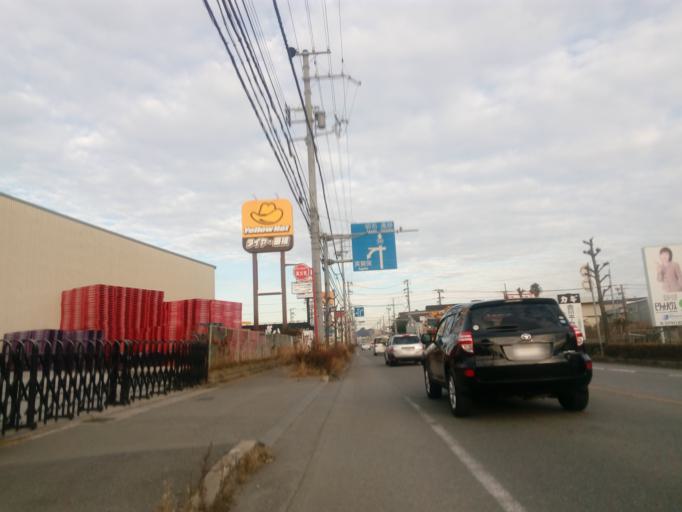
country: JP
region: Hyogo
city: Himeji
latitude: 34.7965
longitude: 134.6505
